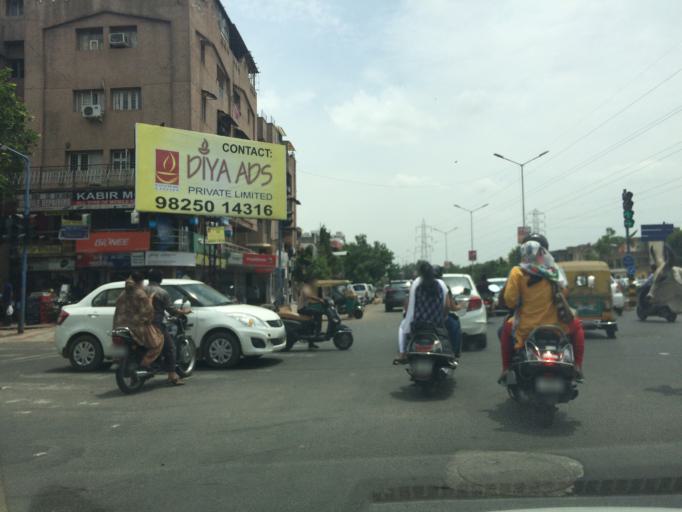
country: IN
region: Gujarat
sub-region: Ahmadabad
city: Ahmedabad
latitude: 23.0618
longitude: 72.5527
